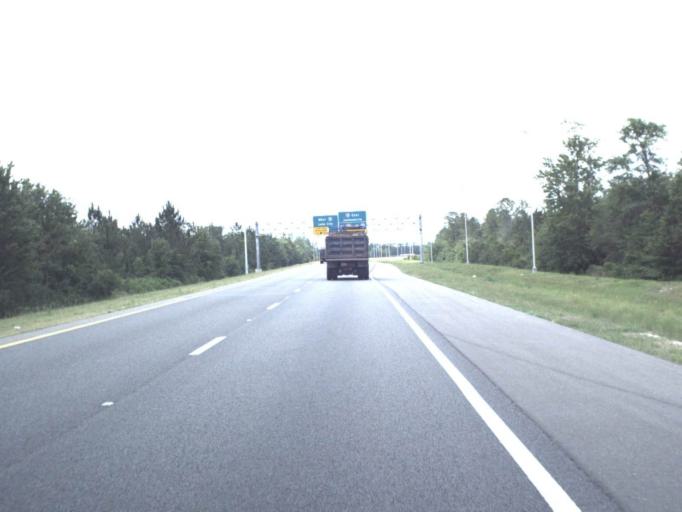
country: US
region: Florida
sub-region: Duval County
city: Baldwin
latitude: 30.2926
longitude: -81.8783
